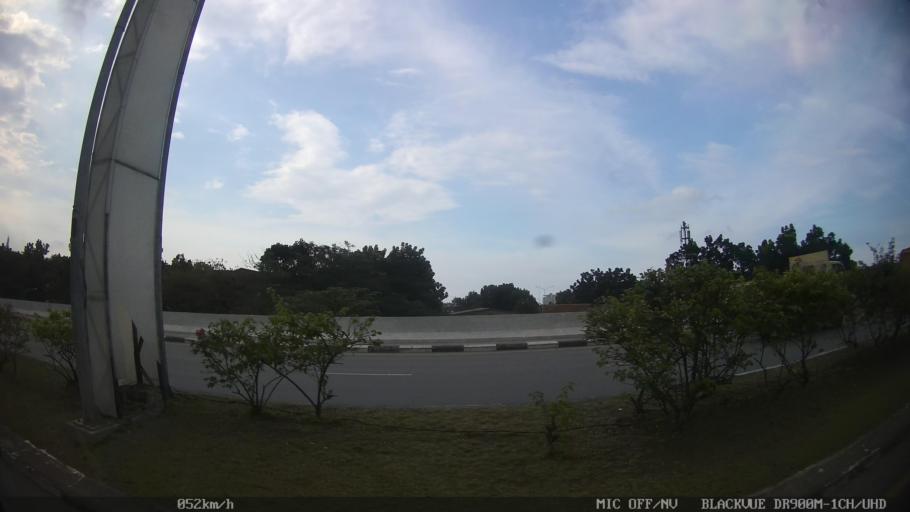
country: ID
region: North Sumatra
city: Medan
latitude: 3.6059
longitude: 98.7226
